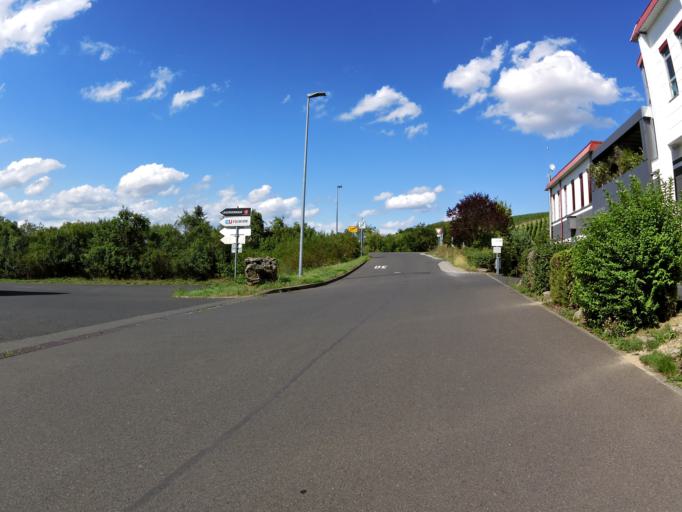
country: DE
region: Bavaria
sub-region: Regierungsbezirk Unterfranken
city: Segnitz
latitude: 49.6795
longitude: 10.1533
